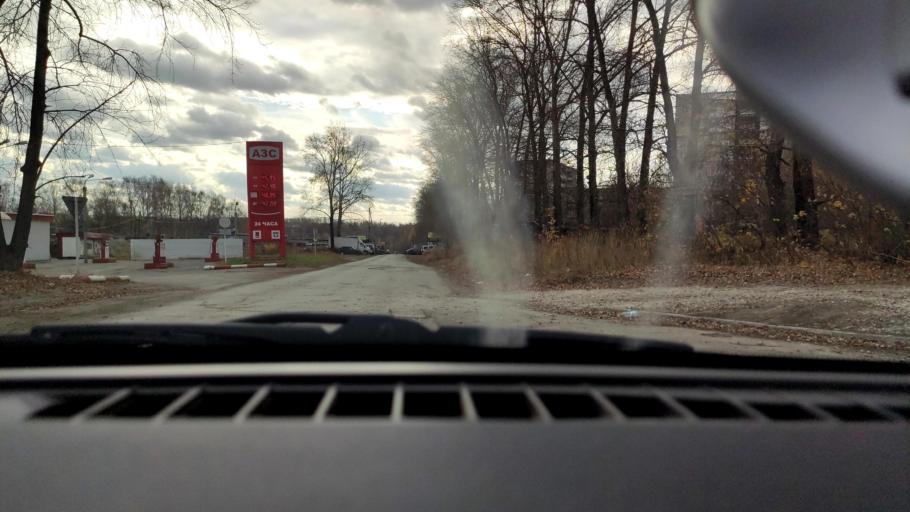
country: RU
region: Perm
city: Perm
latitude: 57.9665
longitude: 56.2029
